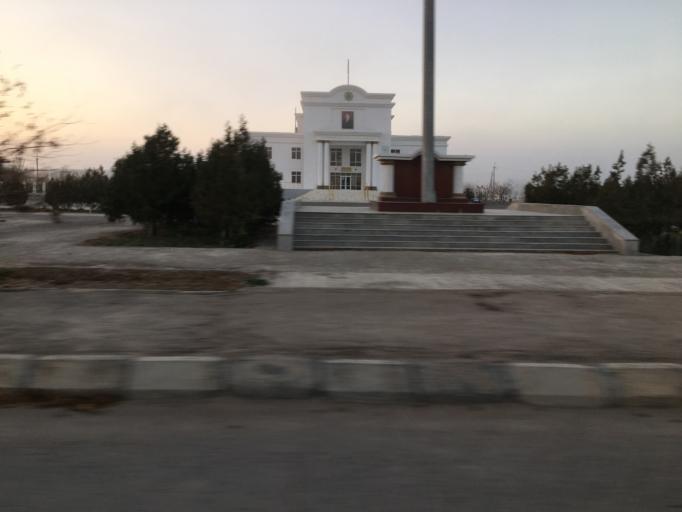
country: TM
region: Dasoguz
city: Koeneuergench
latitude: 41.7423
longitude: 58.6947
